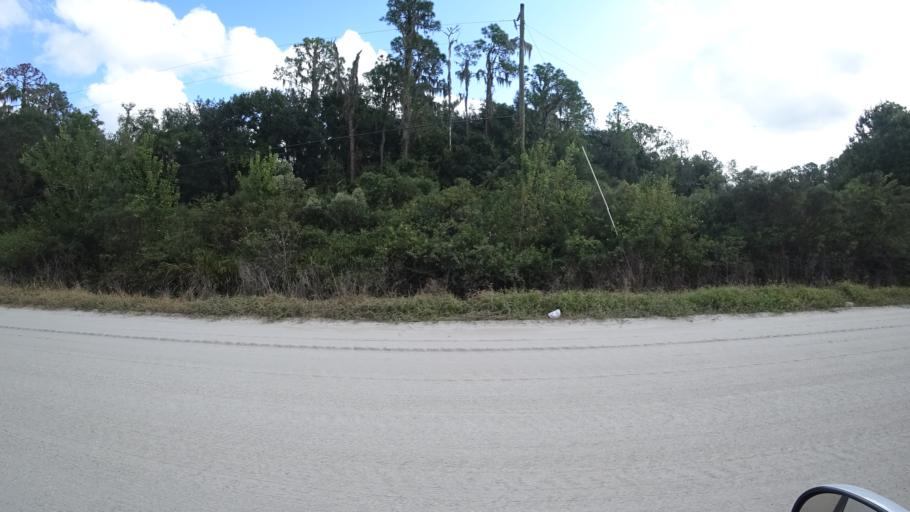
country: US
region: Florida
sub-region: Hillsborough County
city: Wimauma
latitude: 27.4520
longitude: -82.1831
